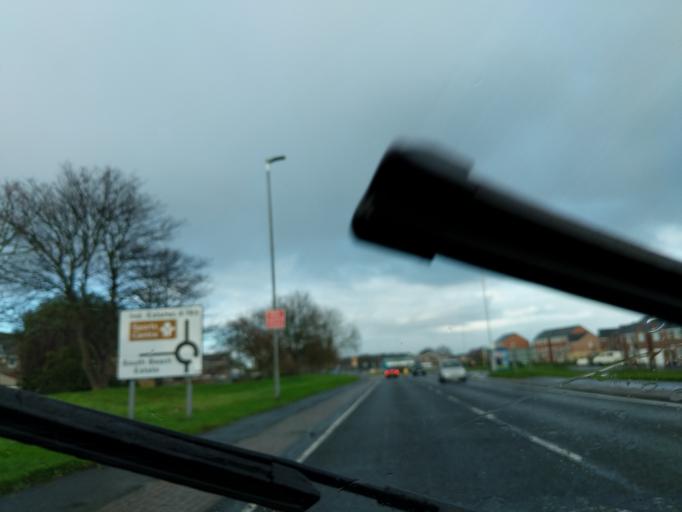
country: GB
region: England
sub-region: Northumberland
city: Blyth
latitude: 55.1137
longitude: -1.5060
